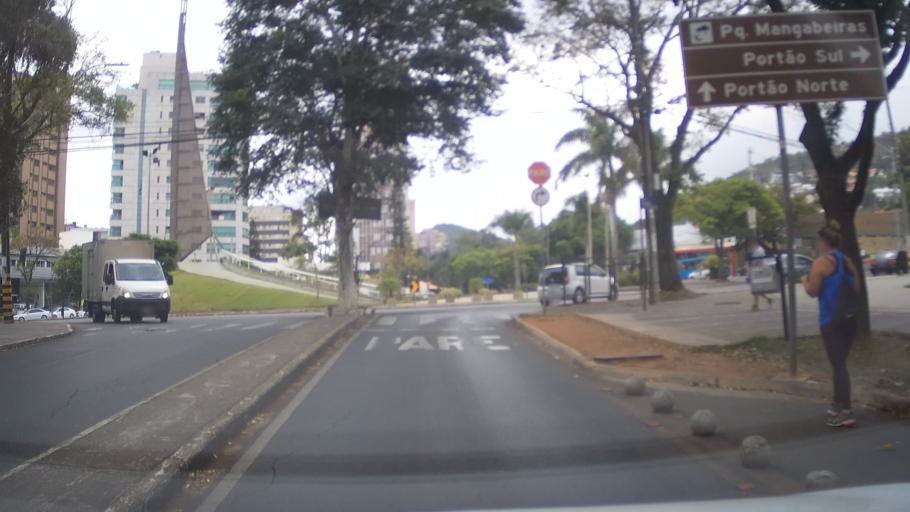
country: BR
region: Minas Gerais
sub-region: Belo Horizonte
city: Belo Horizonte
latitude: -19.9493
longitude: -43.9206
